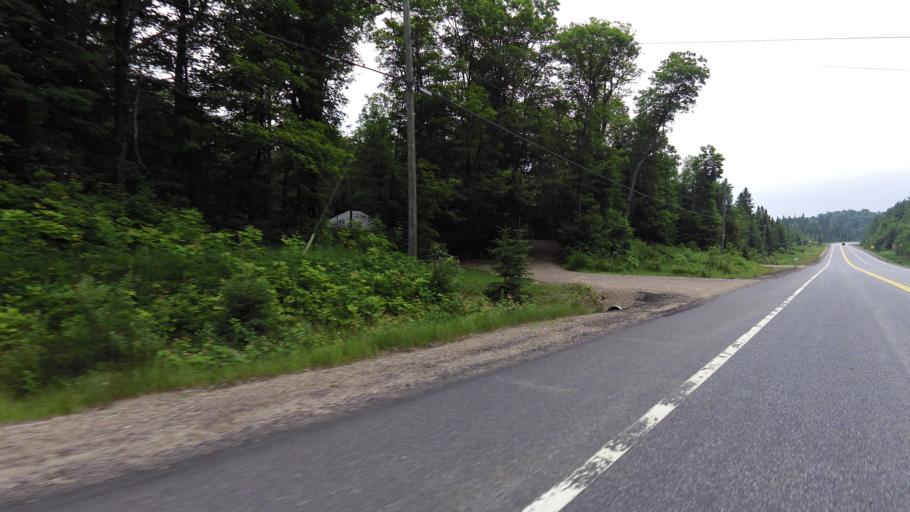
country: CA
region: Ontario
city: Huntsville
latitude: 45.3964
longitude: -78.8903
